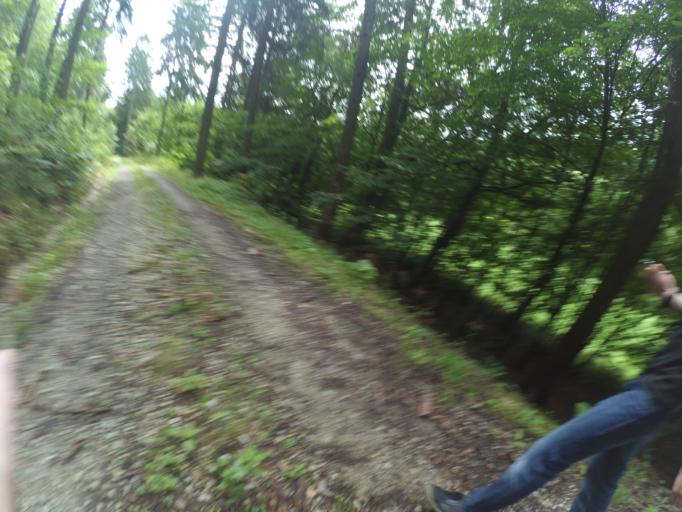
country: DE
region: Hesse
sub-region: Regierungsbezirk Kassel
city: Kirchheim
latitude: 50.8602
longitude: 9.5430
